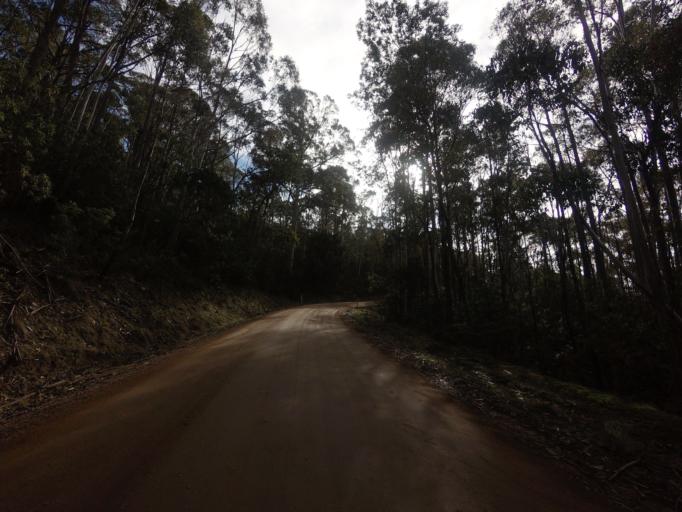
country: AU
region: Tasmania
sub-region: Derwent Valley
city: New Norfolk
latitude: -42.7885
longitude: 146.9372
